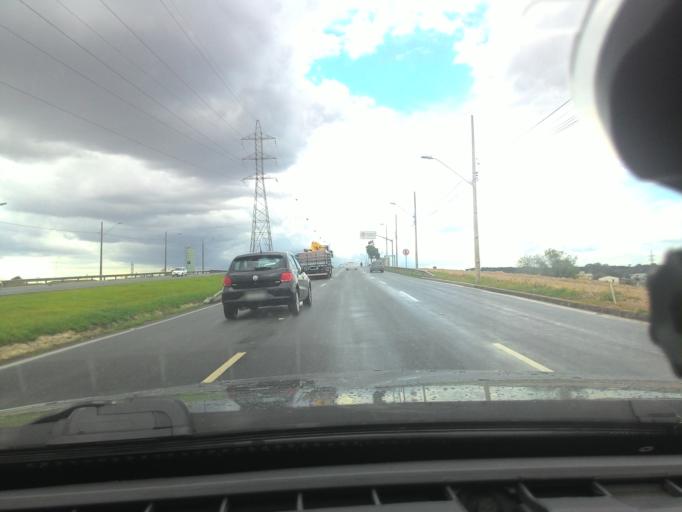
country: BR
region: Parana
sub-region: Sao Jose Dos Pinhais
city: Sao Jose dos Pinhais
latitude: -25.5029
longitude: -49.2075
